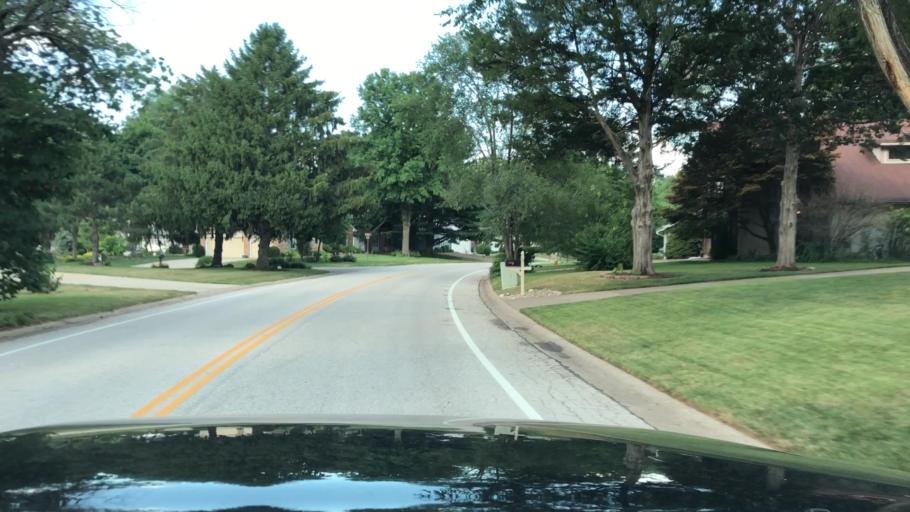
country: US
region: Missouri
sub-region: Saint Charles County
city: Lake Saint Louis
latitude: 38.7963
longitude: -90.7933
